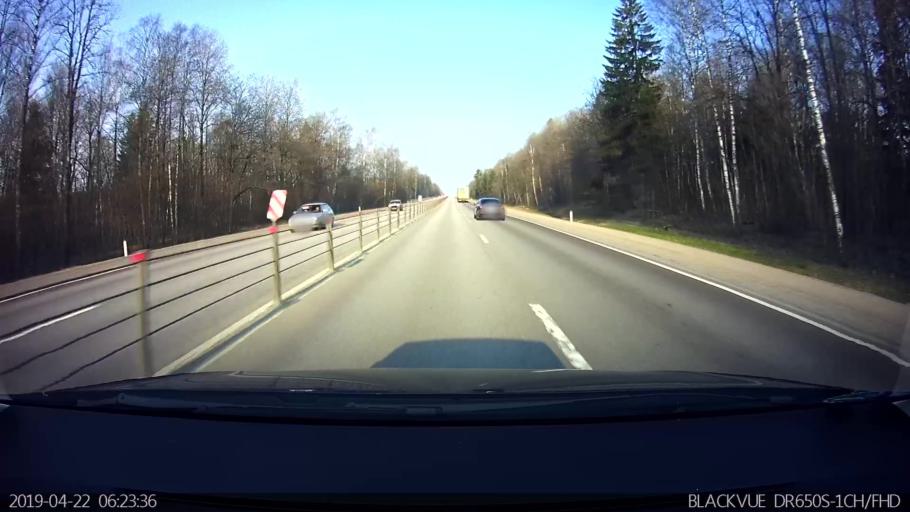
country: RU
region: Moskovskaya
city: Uvarovka
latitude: 55.4651
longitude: 35.8058
